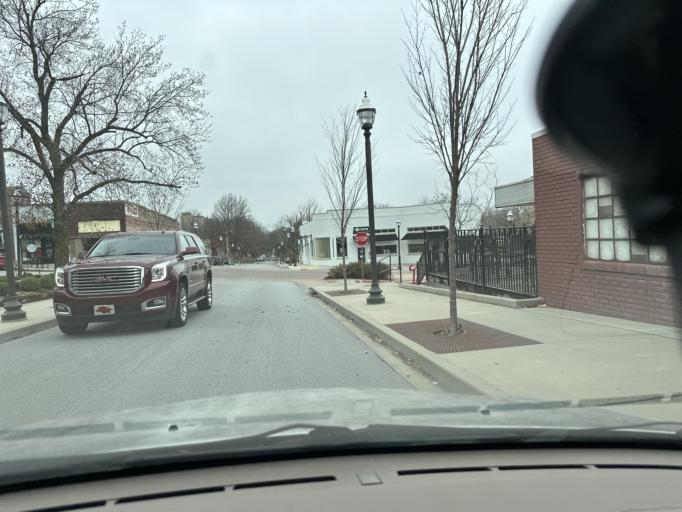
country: US
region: Arkansas
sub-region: Washington County
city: Fayetteville
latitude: 36.0637
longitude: -94.1602
